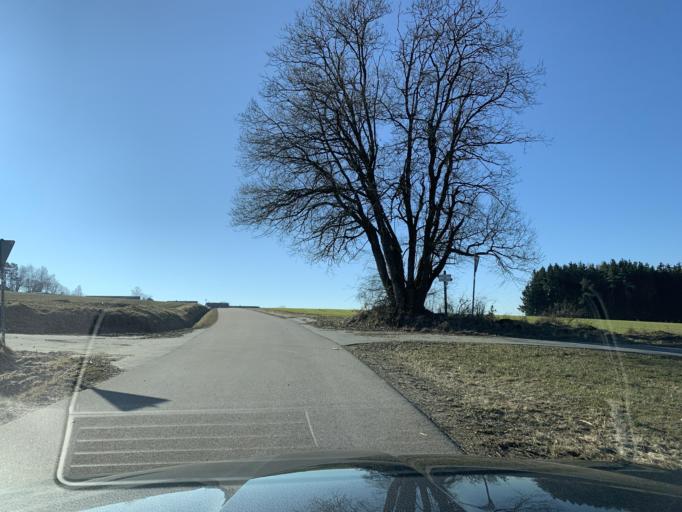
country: DE
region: Bavaria
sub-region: Upper Palatinate
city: Winklarn
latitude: 49.4172
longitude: 12.4491
